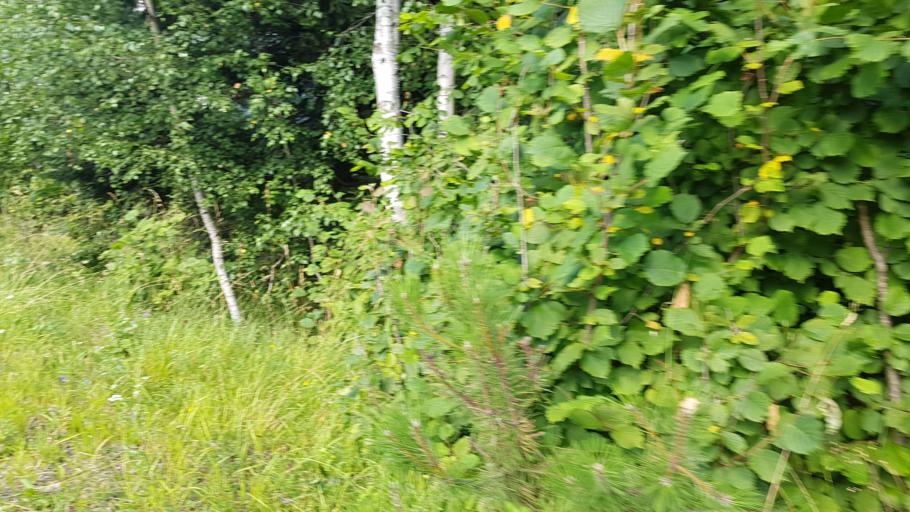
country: IT
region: Friuli Venezia Giulia
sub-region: Provincia di Udine
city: Dogna
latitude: 46.4299
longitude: 13.3058
